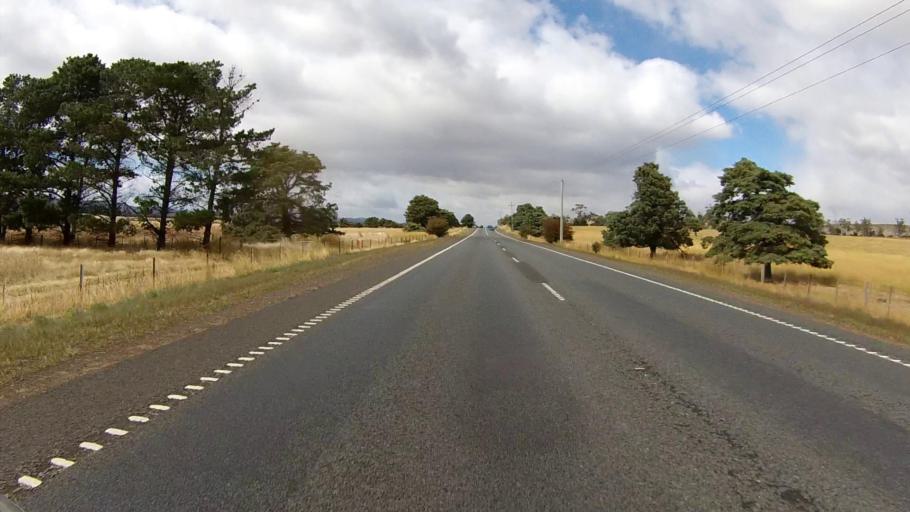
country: AU
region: Tasmania
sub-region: Northern Midlands
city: Evandale
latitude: -41.9505
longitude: 147.4947
